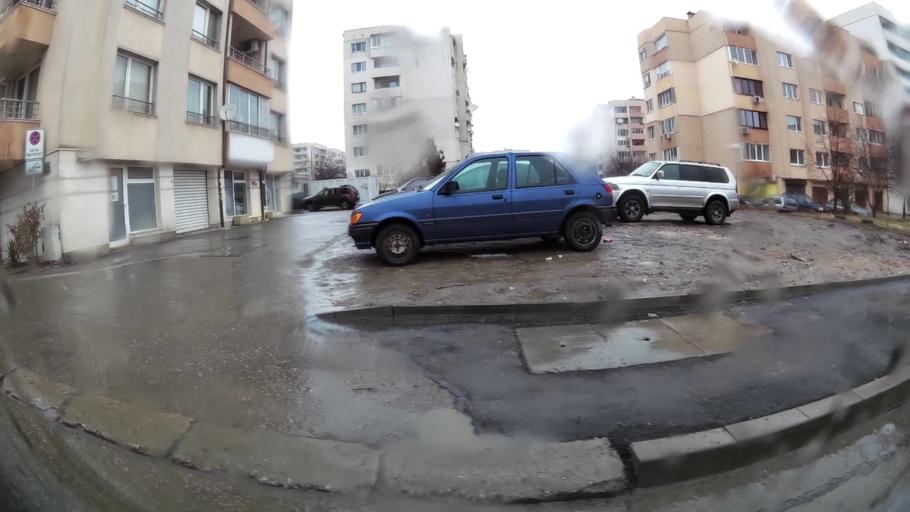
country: BG
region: Sofia-Capital
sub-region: Stolichna Obshtina
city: Sofia
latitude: 42.6500
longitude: 23.3633
